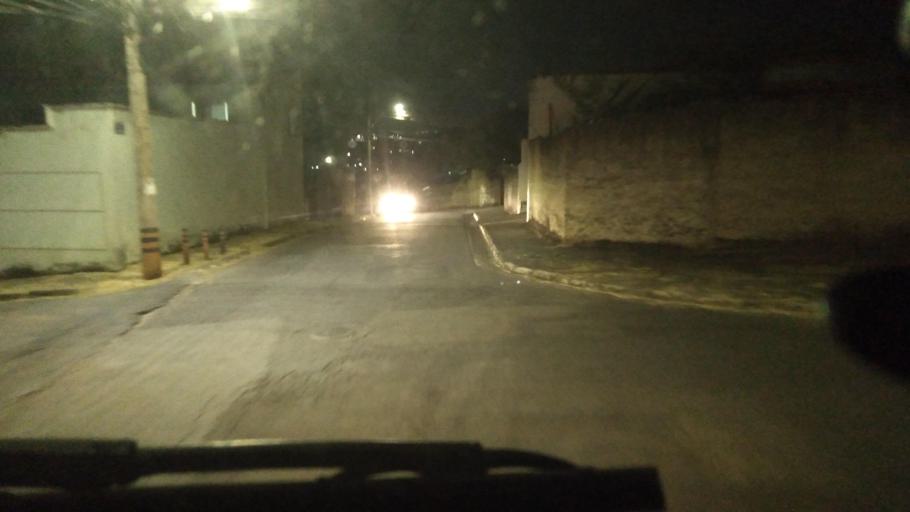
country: BR
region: Minas Gerais
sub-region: Belo Horizonte
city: Belo Horizonte
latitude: -19.8851
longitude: -43.9553
